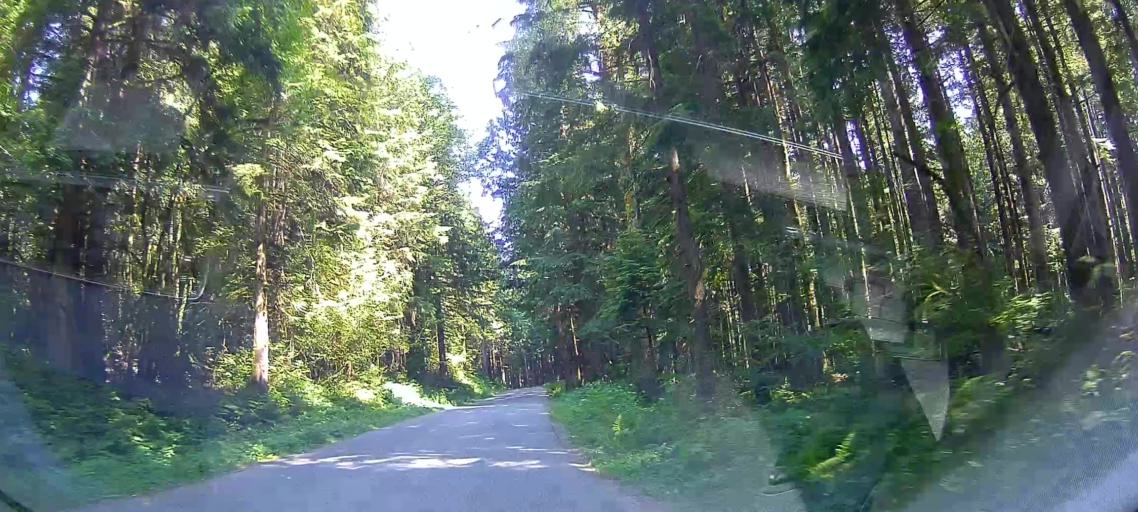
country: US
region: Washington
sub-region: Snohomish County
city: Arlington Heights
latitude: 48.3380
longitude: -122.0314
